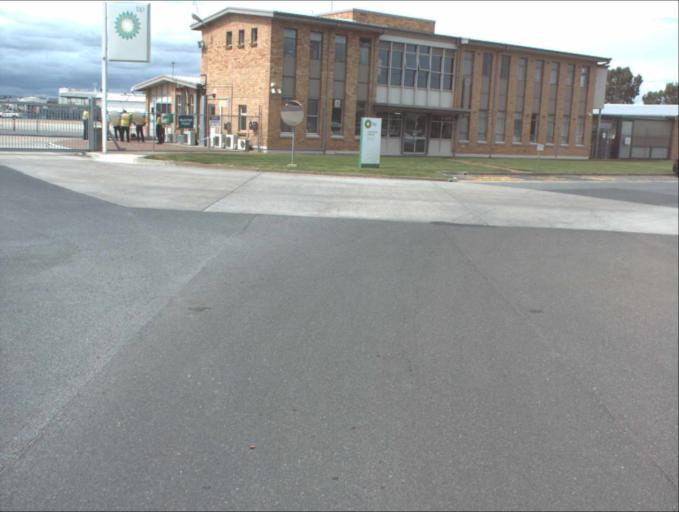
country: AU
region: South Australia
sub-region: Port Adelaide Enfield
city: Birkenhead
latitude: -34.8189
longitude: 138.5027
